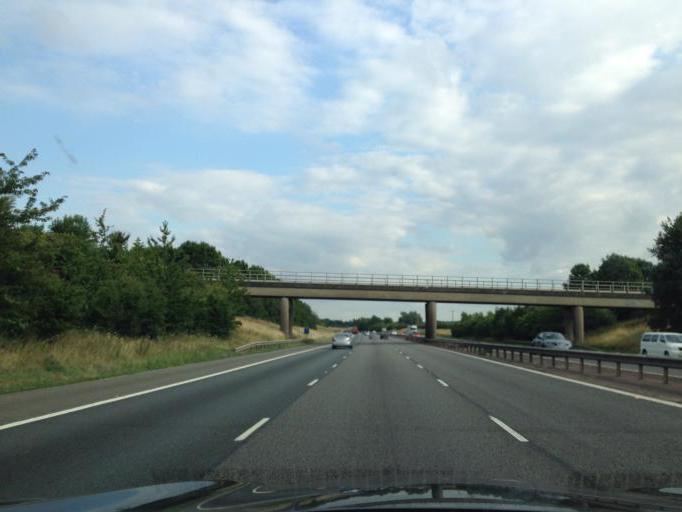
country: GB
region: England
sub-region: Warwickshire
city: Harbury
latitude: 52.1731
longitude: -1.4431
